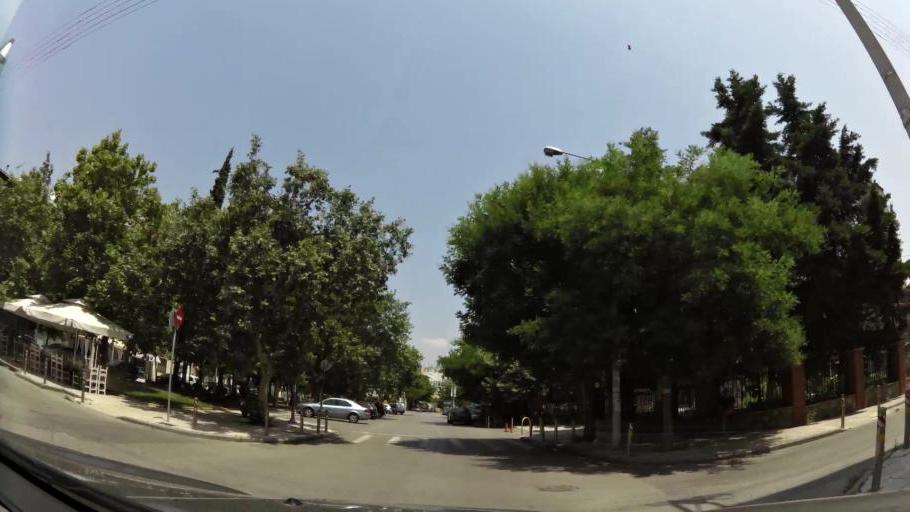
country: GR
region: Central Macedonia
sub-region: Nomos Thessalonikis
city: Menemeni
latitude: 40.6655
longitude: 22.8970
